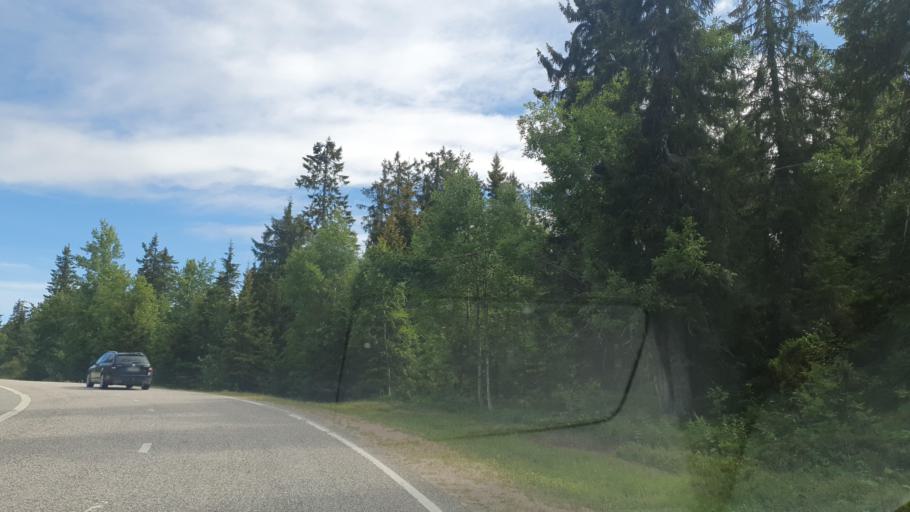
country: FI
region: Kainuu
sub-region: Kajaani
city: Vuokatti
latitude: 64.1285
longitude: 28.2613
